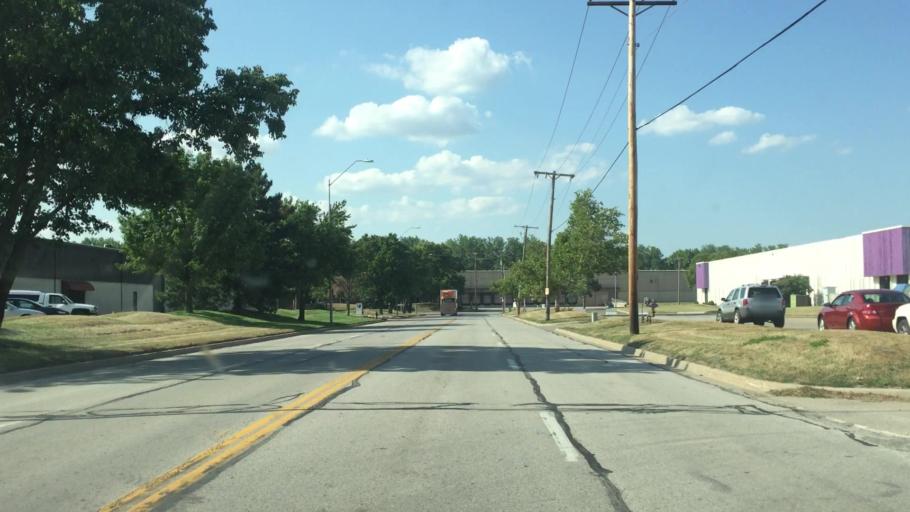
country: US
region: Missouri
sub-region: Clay County
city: North Kansas City
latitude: 39.1420
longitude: -94.5136
